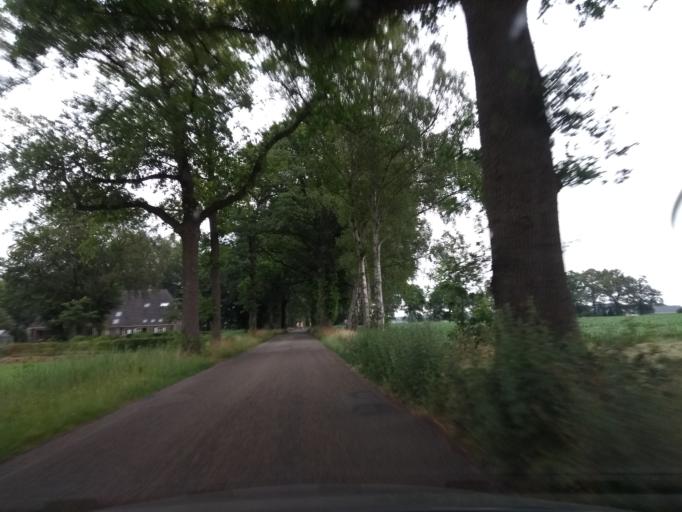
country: NL
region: Gelderland
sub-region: Gemeente Lochem
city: Barchem
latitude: 52.1133
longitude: 6.4097
